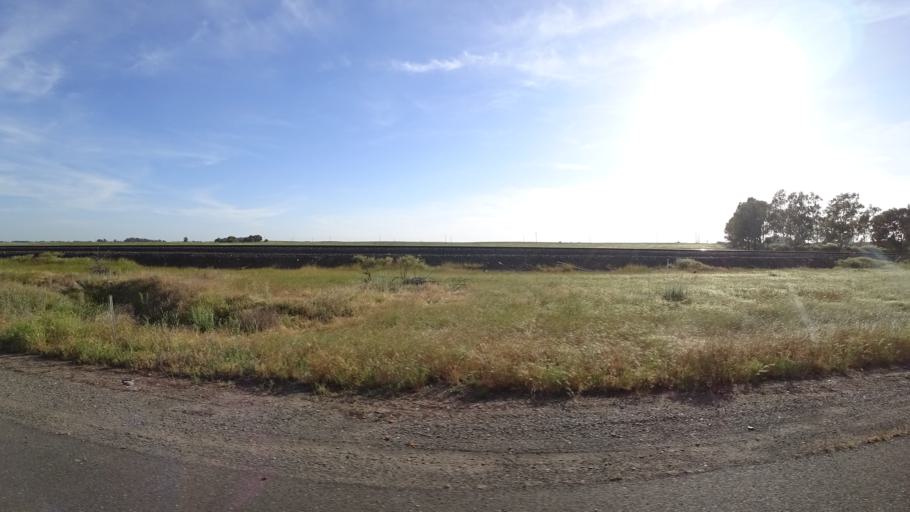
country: US
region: California
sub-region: Placer County
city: Sheridan
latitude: 38.9773
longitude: -121.3737
